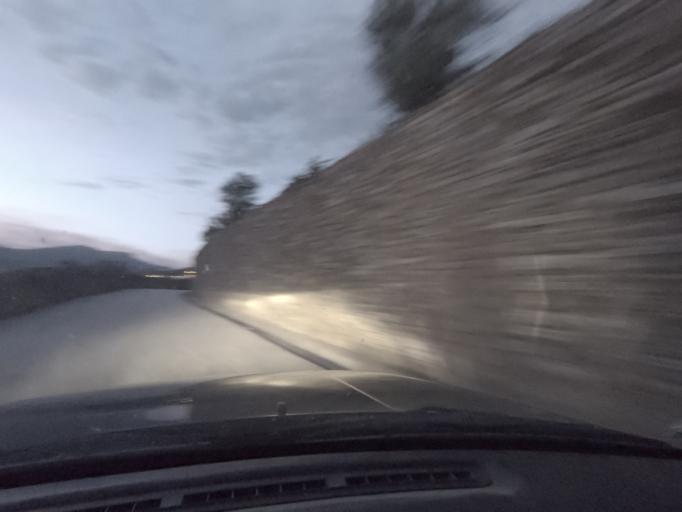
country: PT
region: Vila Real
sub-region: Peso da Regua
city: Godim
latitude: 41.1704
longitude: -7.8299
